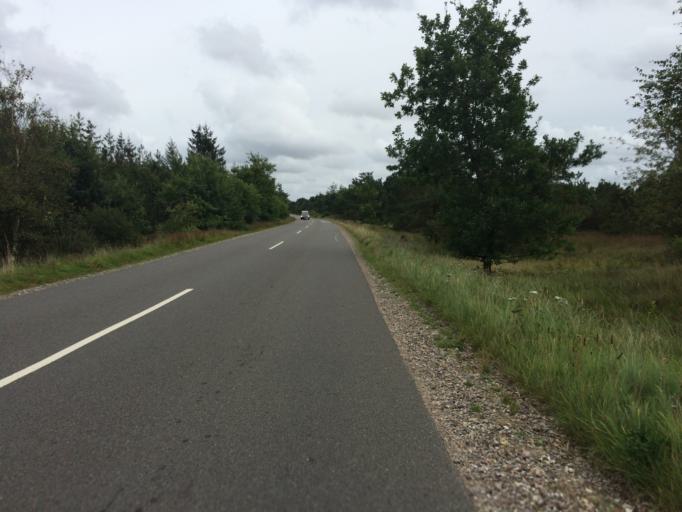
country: DK
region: Central Jutland
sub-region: Holstebro Kommune
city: Ulfborg
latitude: 56.2191
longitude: 8.3876
